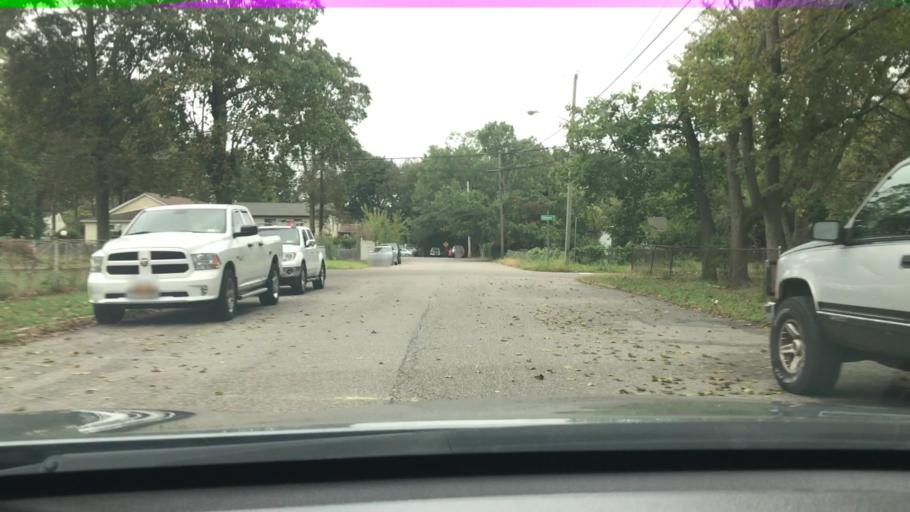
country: US
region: New York
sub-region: Suffolk County
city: West Babylon
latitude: 40.7326
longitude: -73.3642
